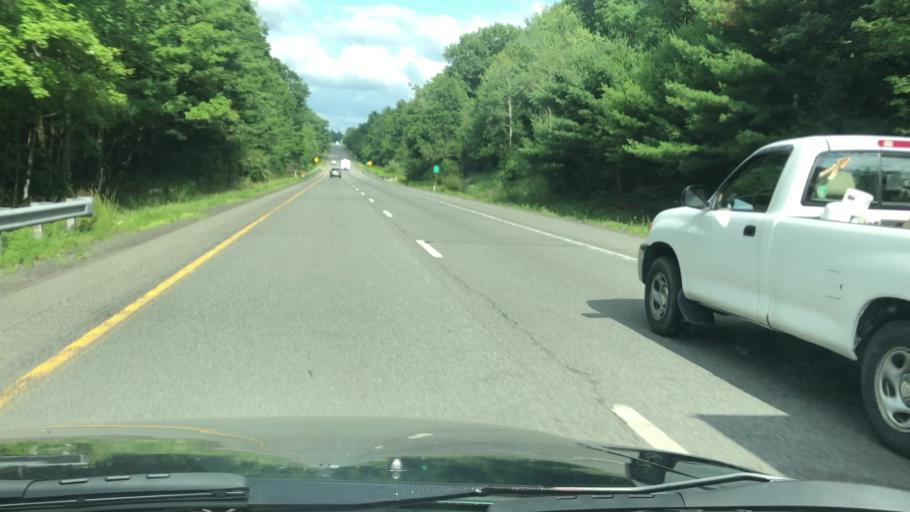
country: US
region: Pennsylvania
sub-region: Pike County
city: Gold Key Lake
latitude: 41.3409
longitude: -74.8950
